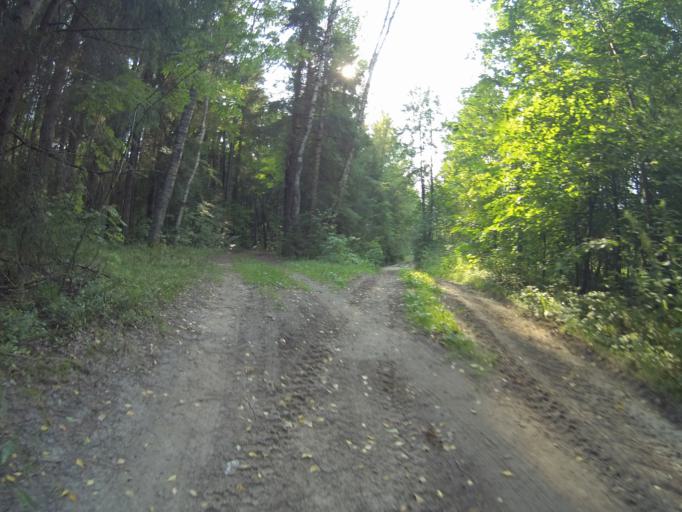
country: RU
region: Vladimir
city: Kommunar
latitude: 56.0490
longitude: 40.5684
